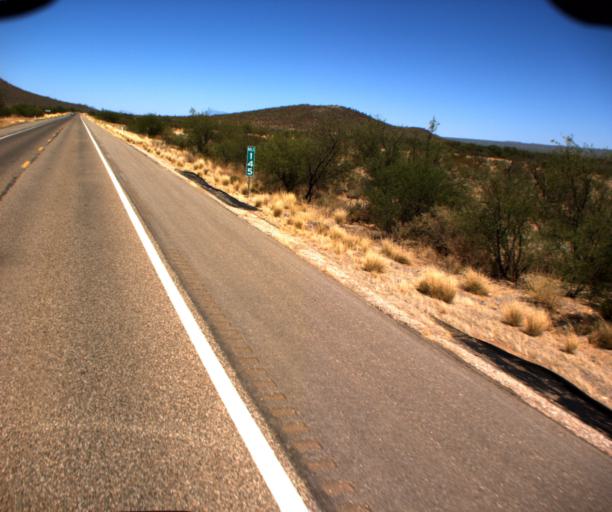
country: US
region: Arizona
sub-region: Pima County
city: Three Points
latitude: 32.0572
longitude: -111.4030
